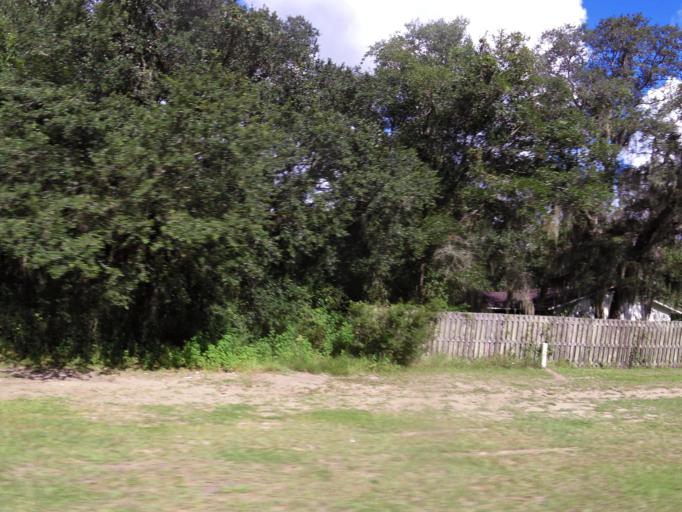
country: US
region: Georgia
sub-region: Camden County
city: Kingsland
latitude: 30.7779
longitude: -81.6867
